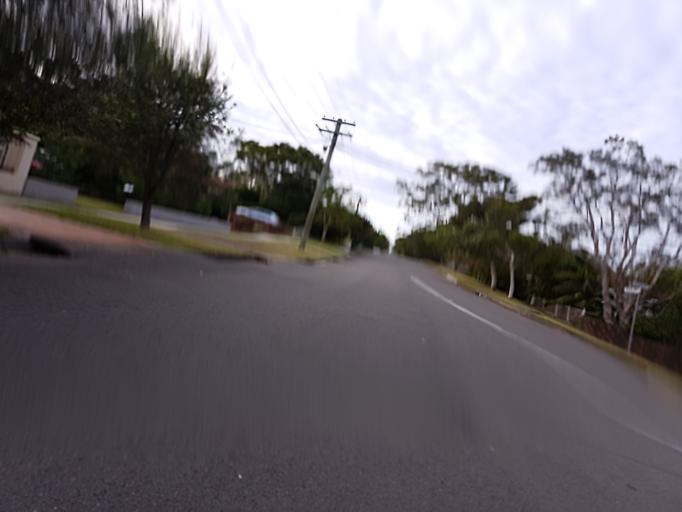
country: AU
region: New South Wales
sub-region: Ku-ring-gai
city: Roseville Chase
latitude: -33.7801
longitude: 151.2010
